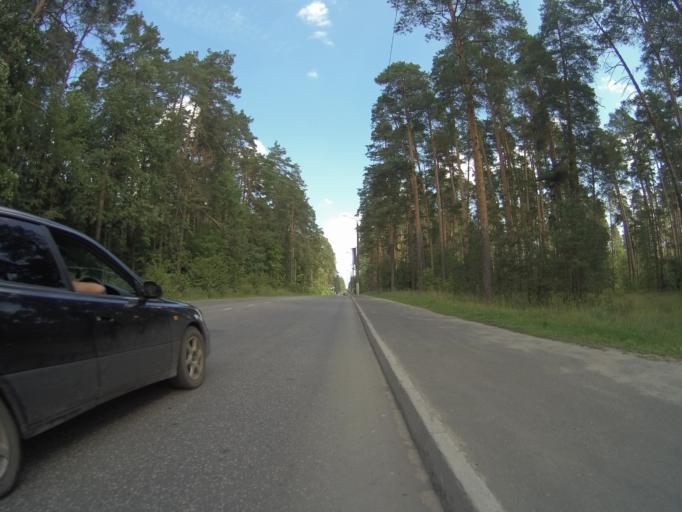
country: RU
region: Vladimir
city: Gus'-Khrustal'nyy
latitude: 55.6298
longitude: 40.6903
